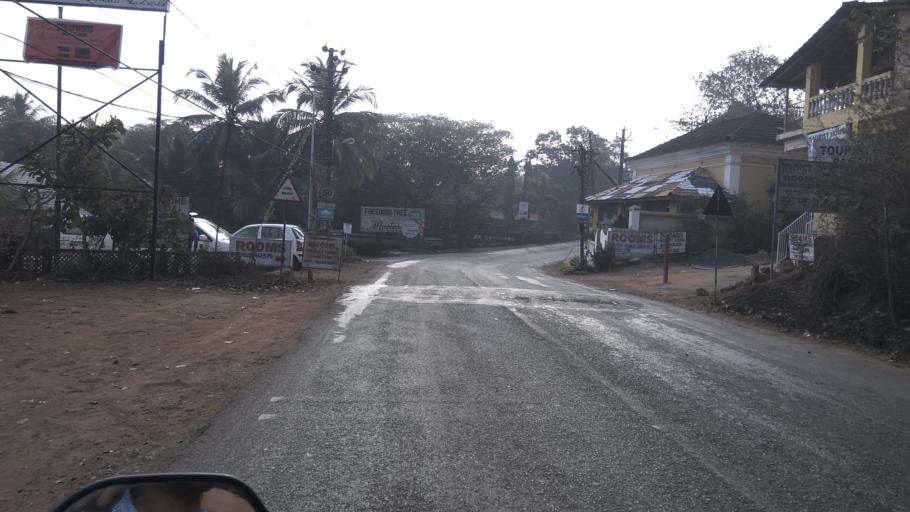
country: IN
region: Goa
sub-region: North Goa
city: Saligao
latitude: 15.5454
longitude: 73.8053
